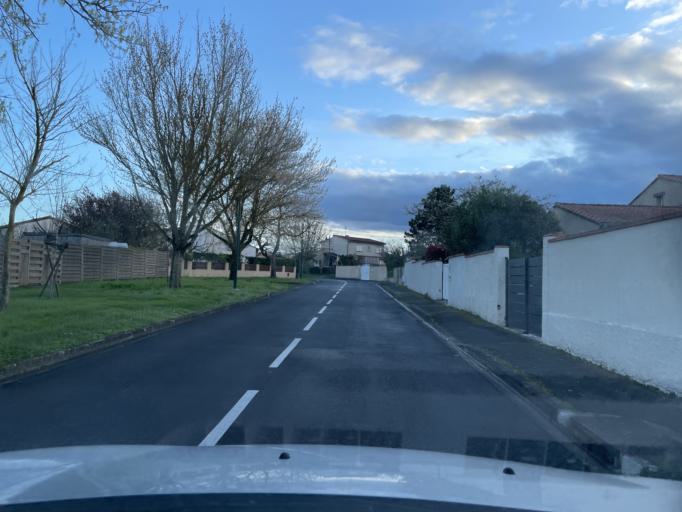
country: FR
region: Midi-Pyrenees
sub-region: Departement de la Haute-Garonne
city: Pibrac
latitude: 43.6133
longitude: 1.2873
